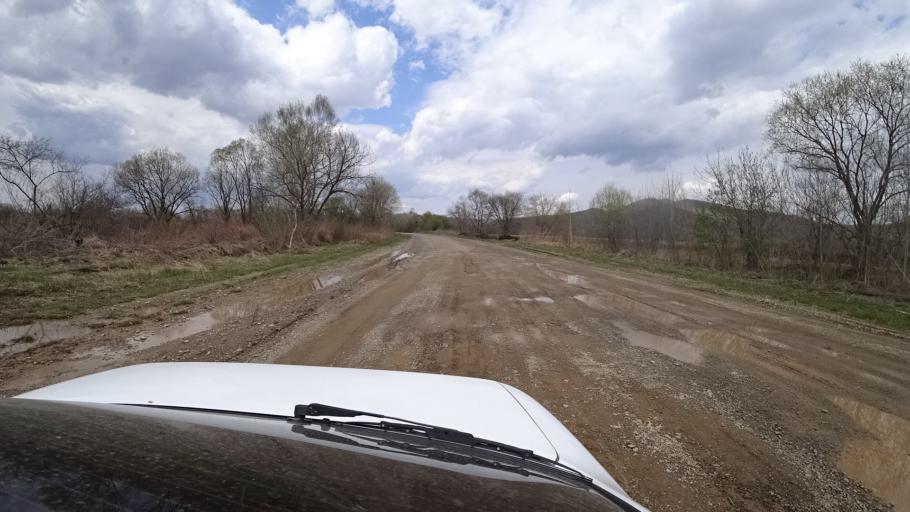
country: RU
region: Primorskiy
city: Novopokrovka
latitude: 45.6127
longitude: 134.2744
